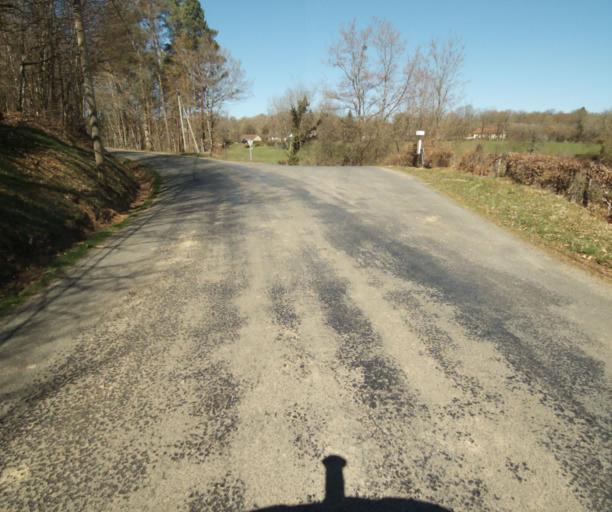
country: FR
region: Limousin
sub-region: Departement de la Correze
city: Saint-Clement
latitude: 45.3176
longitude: 1.6959
